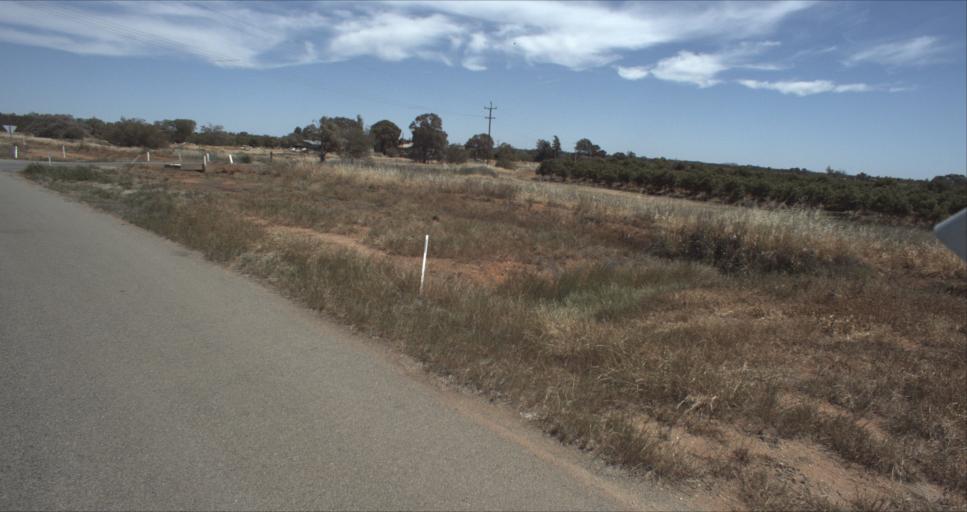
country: AU
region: New South Wales
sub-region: Leeton
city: Leeton
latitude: -34.5950
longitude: 146.4401
